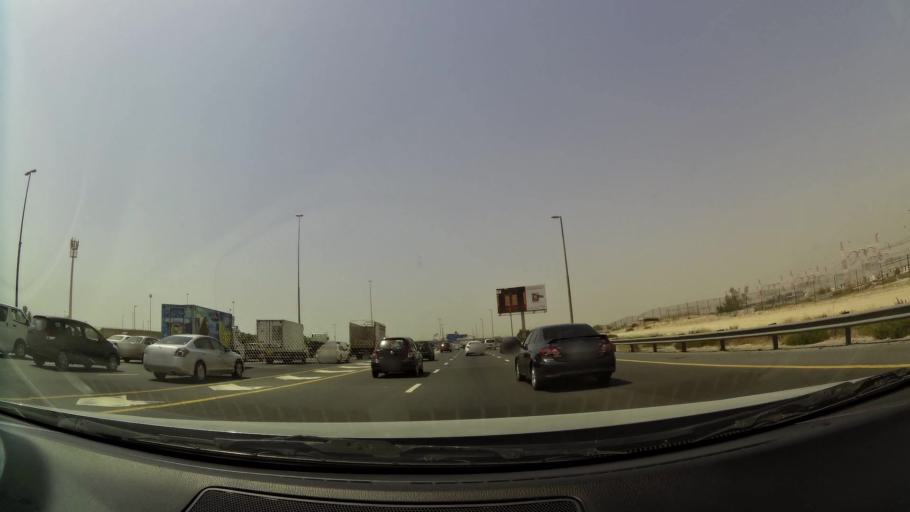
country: AE
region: Ash Shariqah
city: Sharjah
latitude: 25.2257
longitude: 55.4048
